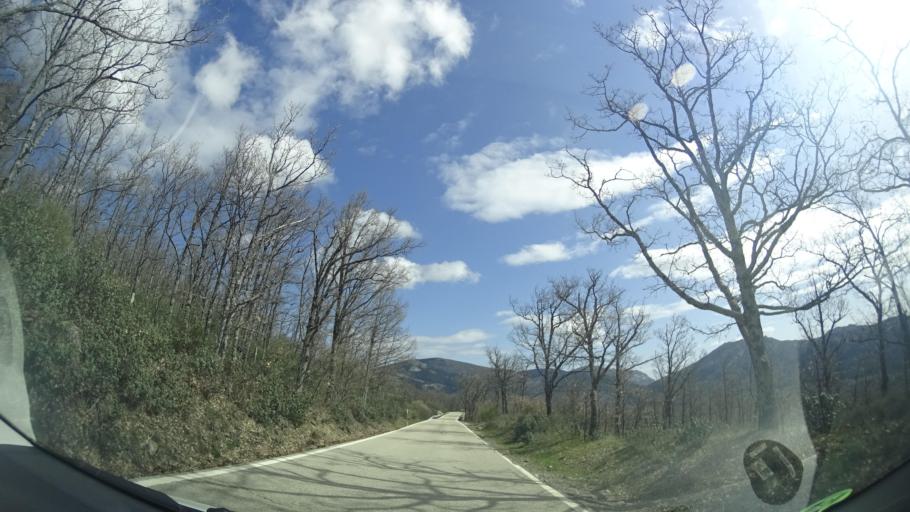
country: ES
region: Madrid
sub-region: Provincia de Madrid
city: Miraflores de la Sierra
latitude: 40.8357
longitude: -3.7699
